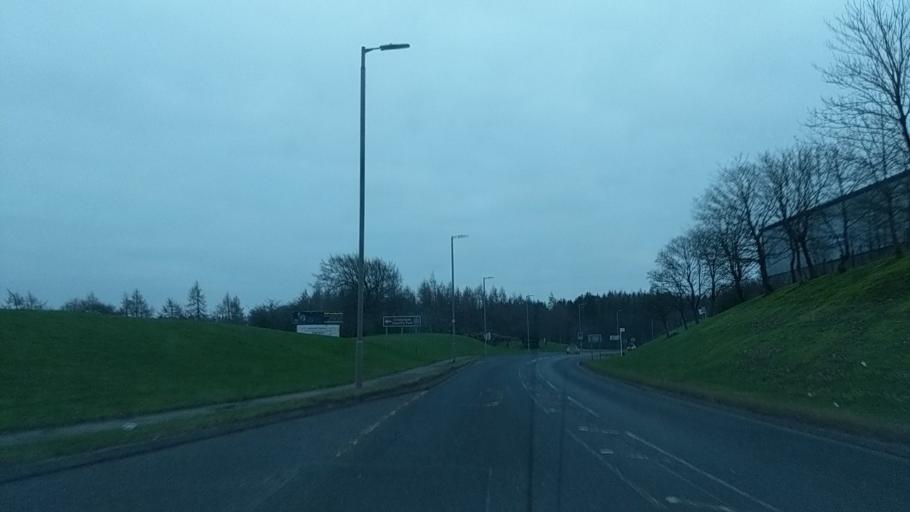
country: GB
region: Scotland
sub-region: South Lanarkshire
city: East Kilbride
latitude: 55.7516
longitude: -4.1536
